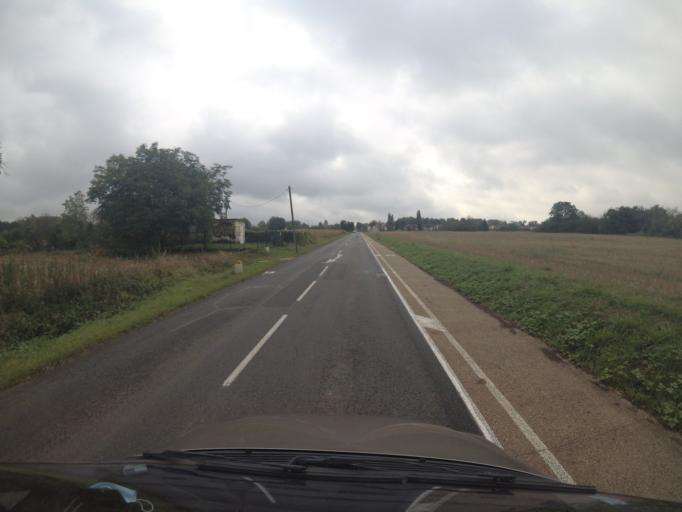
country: FR
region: Ile-de-France
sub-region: Departement de Seine-et-Marne
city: Guermantes
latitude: 48.8586
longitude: 2.7036
